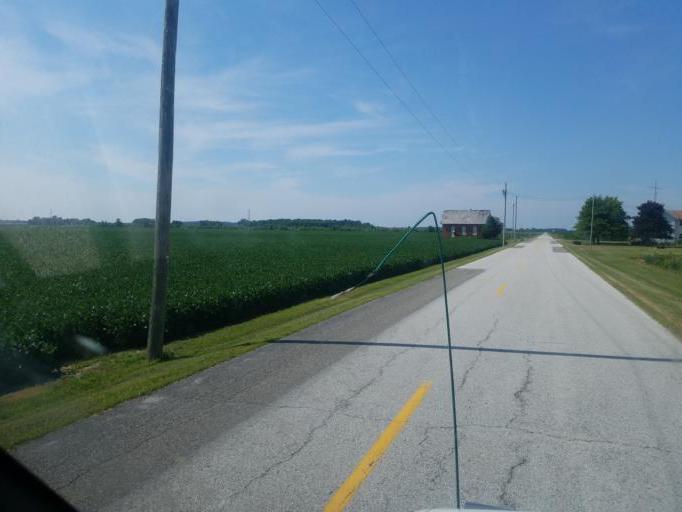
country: US
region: Ohio
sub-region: Logan County
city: Lakeview
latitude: 40.5470
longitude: -84.0120
